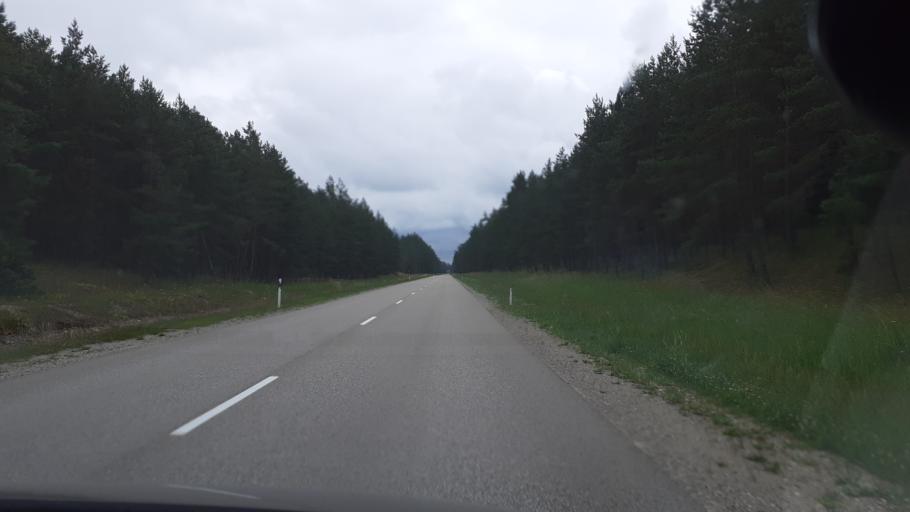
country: LV
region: Ventspils Rajons
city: Piltene
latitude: 57.1160
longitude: 21.7525
